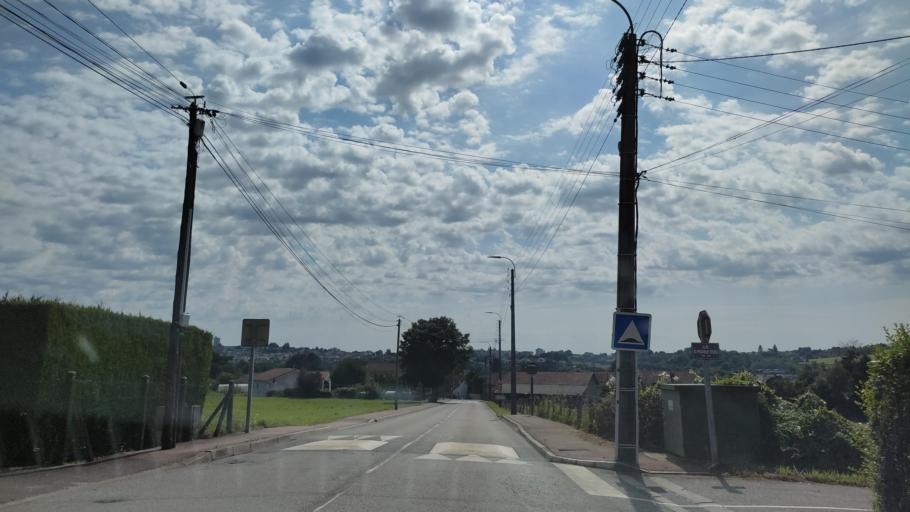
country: FR
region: Limousin
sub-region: Departement de la Haute-Vienne
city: Isle
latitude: 45.8273
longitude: 1.2007
